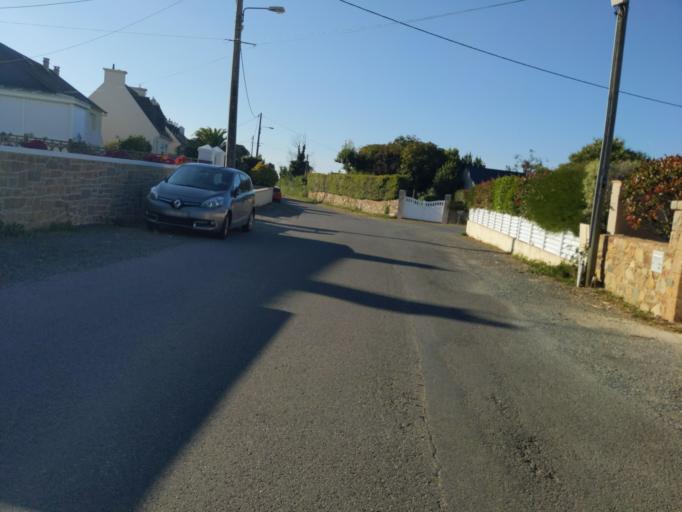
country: FR
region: Brittany
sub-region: Departement des Cotes-d'Armor
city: Pleubian
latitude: 48.8495
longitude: -3.1388
